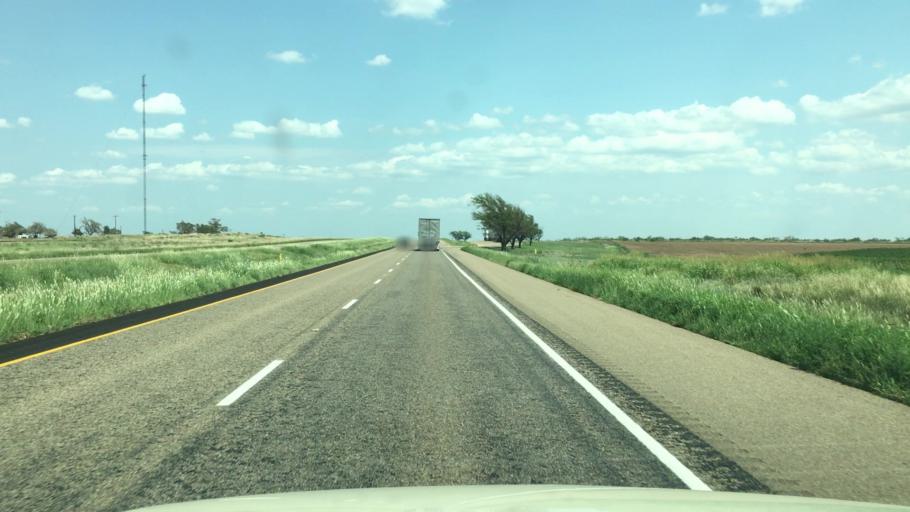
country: US
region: Texas
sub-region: Armstrong County
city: Claude
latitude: 35.0328
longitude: -101.1546
